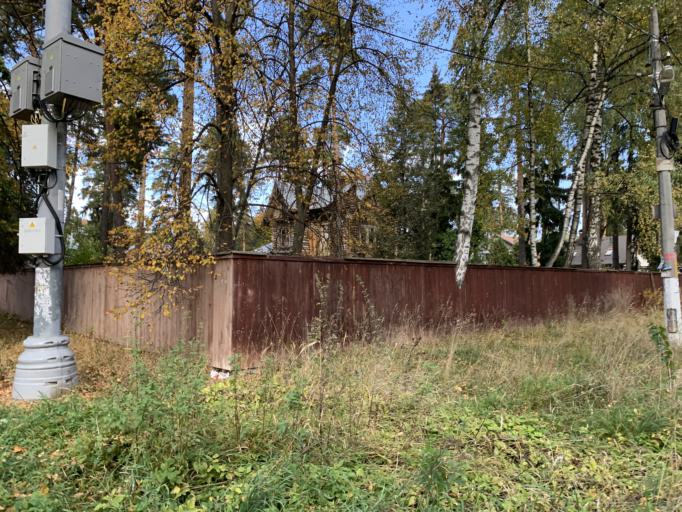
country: RU
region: Moskovskaya
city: Mamontovka
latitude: 55.9795
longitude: 37.8316
